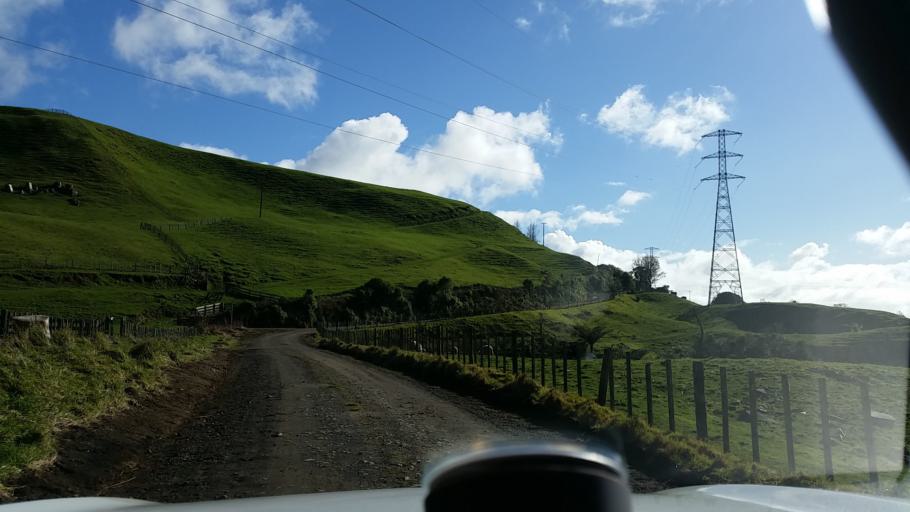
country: NZ
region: Taranaki
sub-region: South Taranaki District
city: Eltham
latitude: -39.4579
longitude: 174.3699
